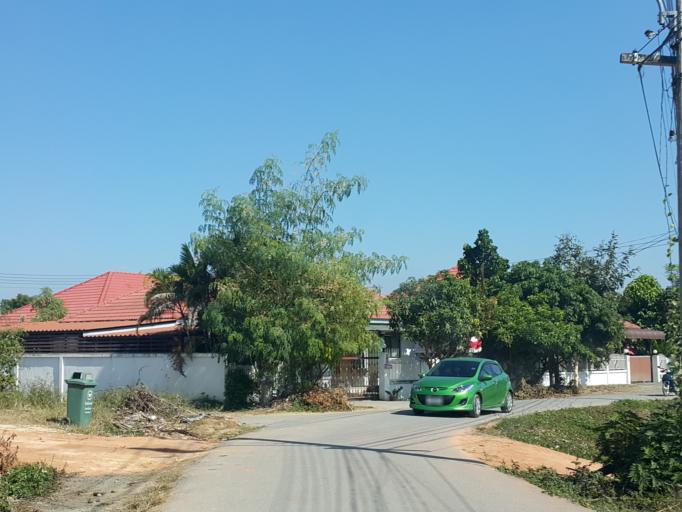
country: TH
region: Chiang Mai
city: San Sai
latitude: 18.8523
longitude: 98.9977
